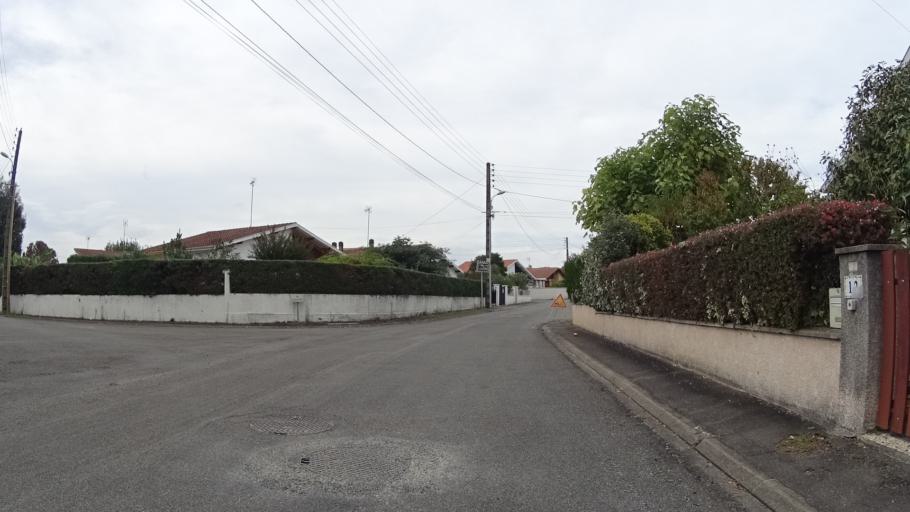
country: FR
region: Aquitaine
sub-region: Departement des Landes
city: Saint-Paul-les-Dax
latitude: 43.7303
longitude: -1.0745
